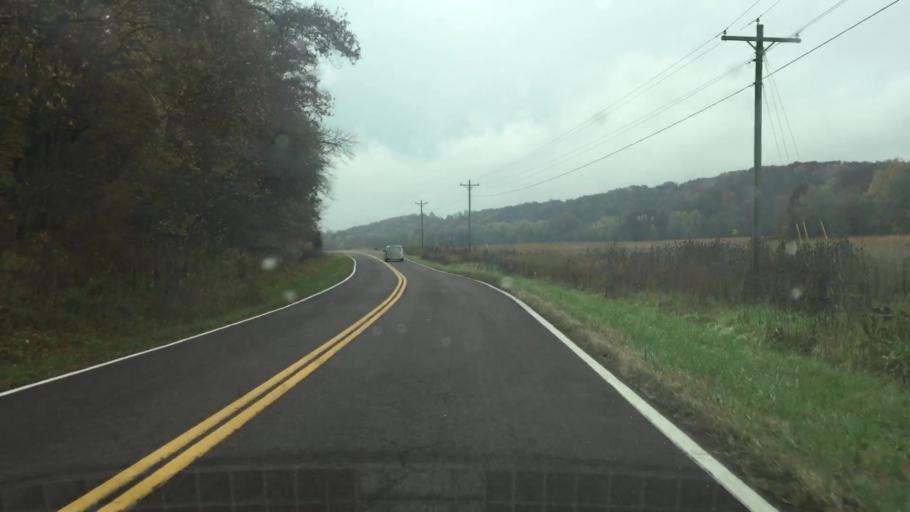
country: US
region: Missouri
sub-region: Callaway County
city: Fulton
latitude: 38.7867
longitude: -91.8559
